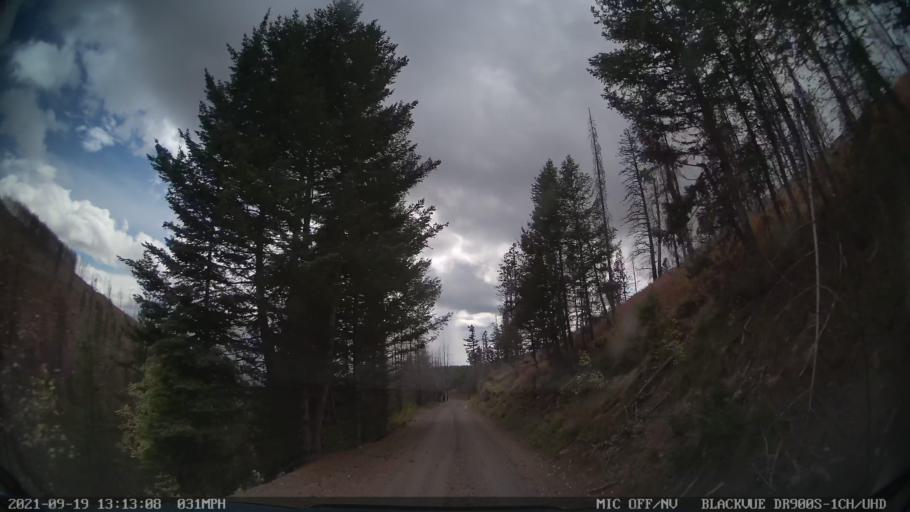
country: US
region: Montana
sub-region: Missoula County
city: Seeley Lake
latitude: 47.1770
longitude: -113.3584
